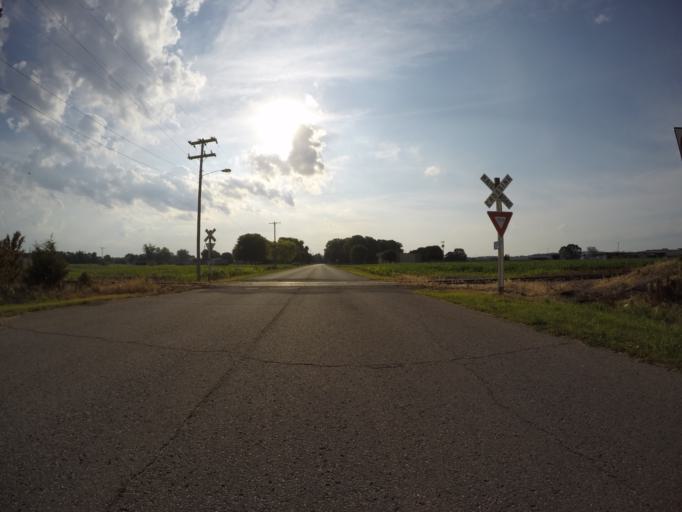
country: US
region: Kansas
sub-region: Doniphan County
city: Elwood
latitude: 39.7517
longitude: -94.8838
